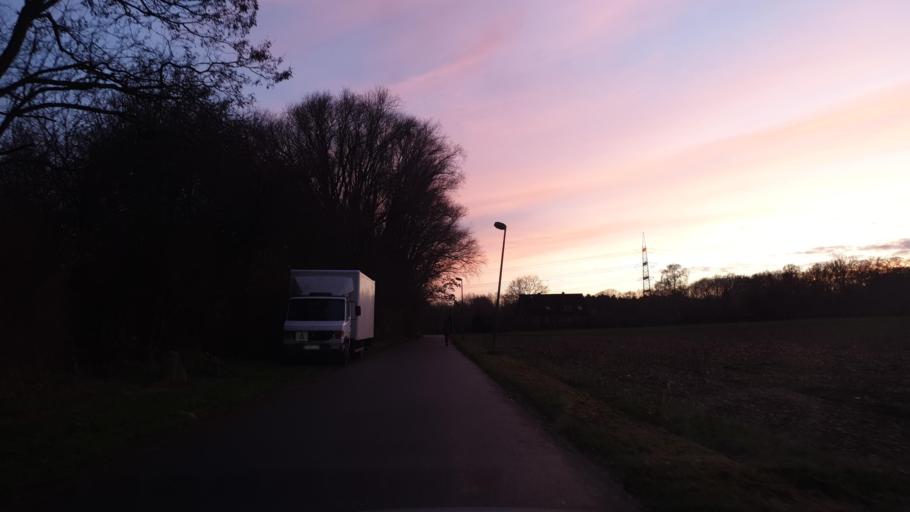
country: DE
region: Lower Saxony
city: Osnabrueck
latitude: 52.2535
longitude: 8.0344
